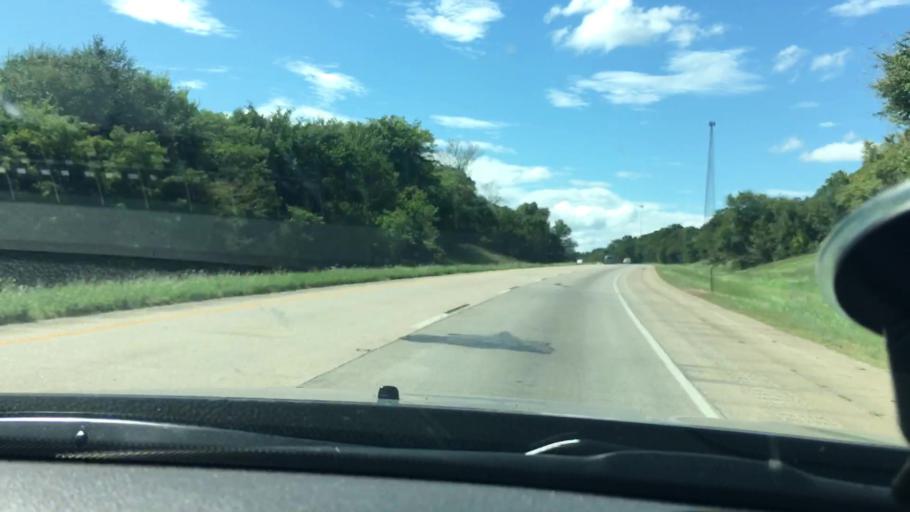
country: US
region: Oklahoma
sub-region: Sequoyah County
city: Vian
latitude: 35.4909
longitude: -94.9978
